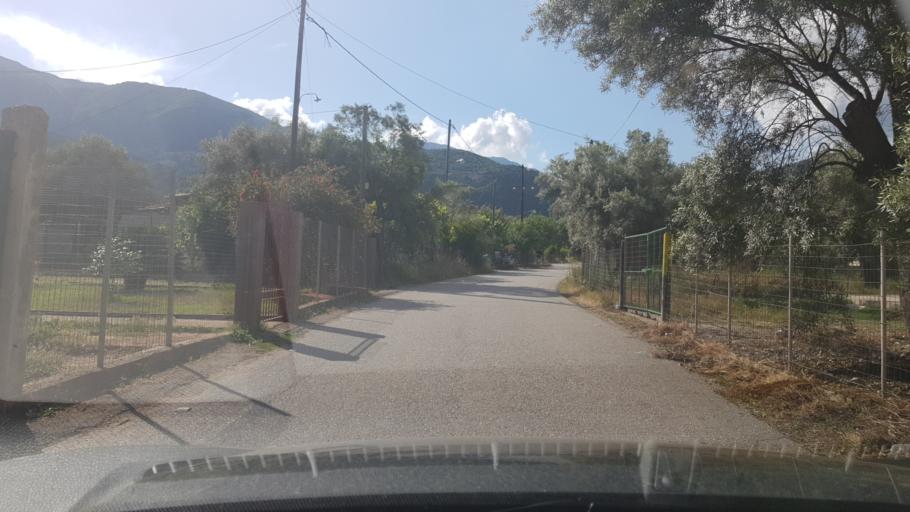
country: GR
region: Ionian Islands
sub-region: Lefkada
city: Nidri
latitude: 38.7114
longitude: 20.7046
